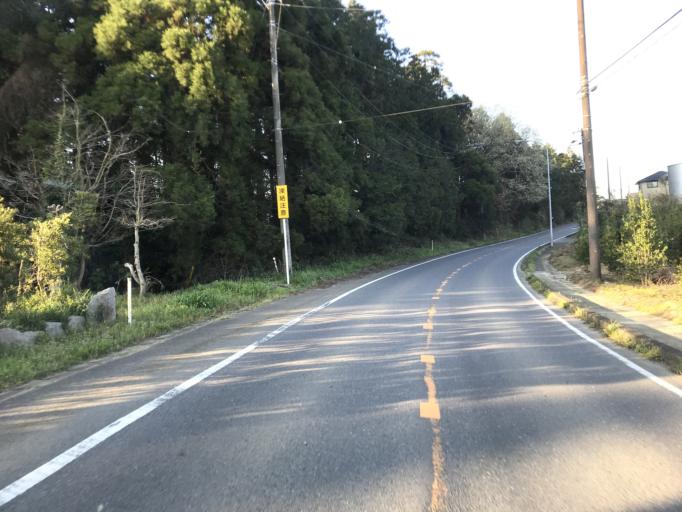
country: JP
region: Chiba
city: Yokaichiba
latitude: 35.7532
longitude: 140.5665
